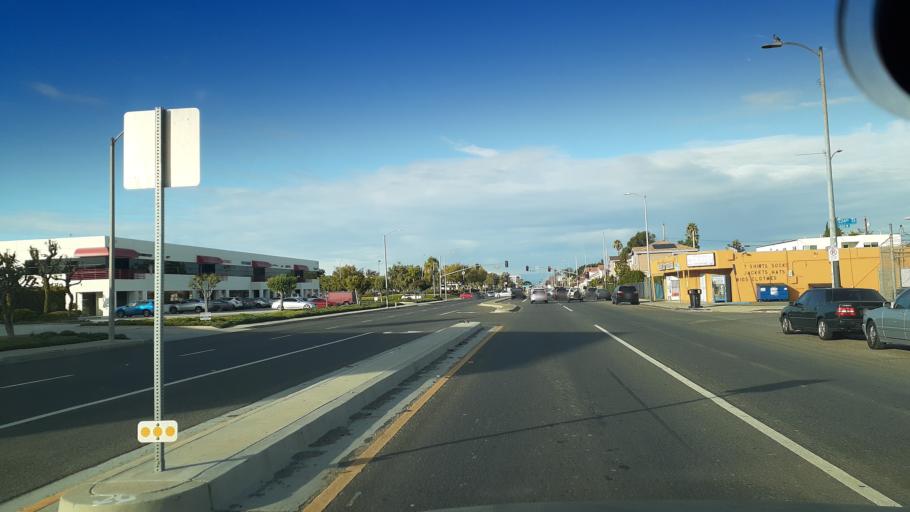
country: US
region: California
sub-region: Los Angeles County
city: West Carson
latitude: 33.8230
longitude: -118.3089
